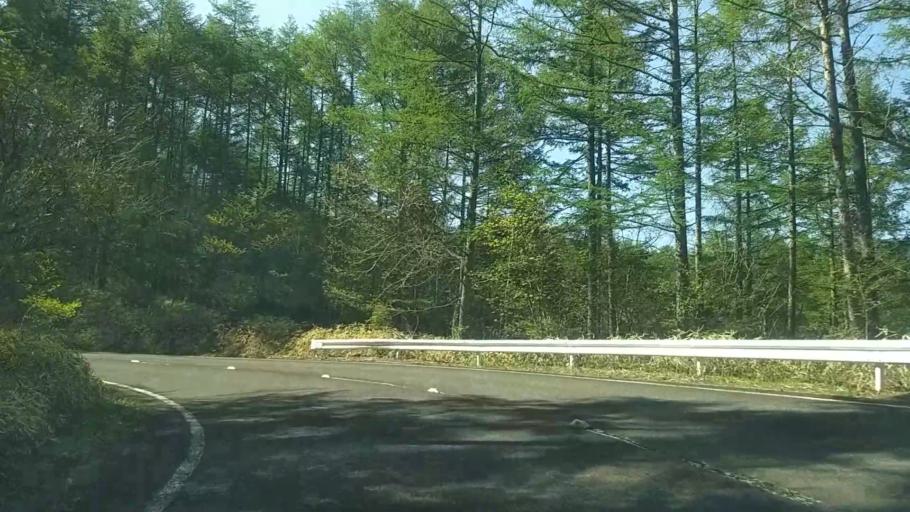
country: JP
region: Yamanashi
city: Nirasaki
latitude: 35.9245
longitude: 138.4003
